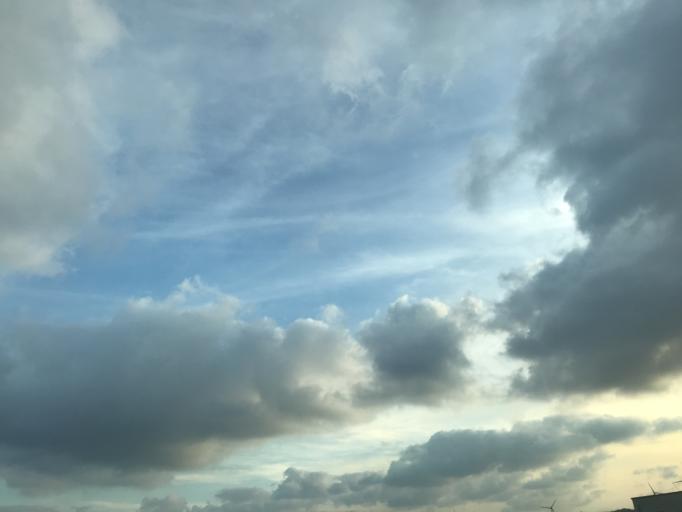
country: TR
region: Istanbul
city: Durusu
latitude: 41.2631
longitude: 28.7142
